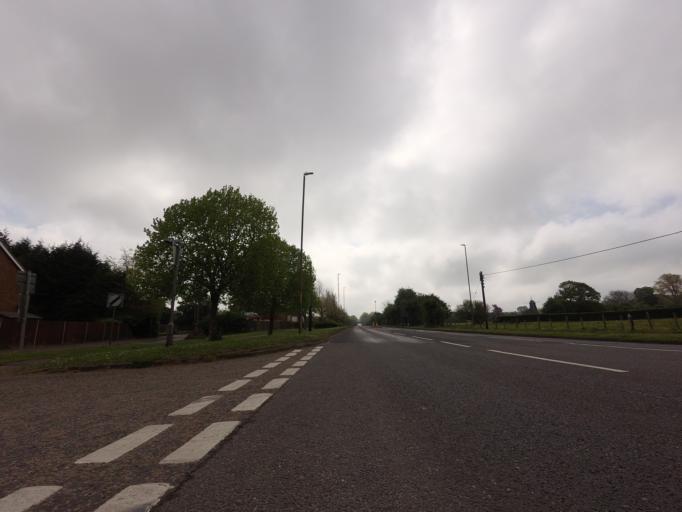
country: GB
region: England
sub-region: Kent
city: Kemsing
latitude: 51.3396
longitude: 0.2690
